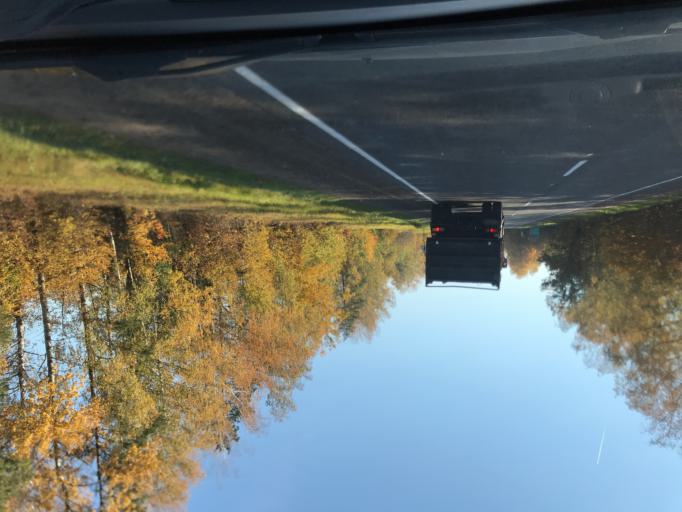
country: BY
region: Mogilev
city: Hlusha
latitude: 53.0916
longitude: 28.9189
